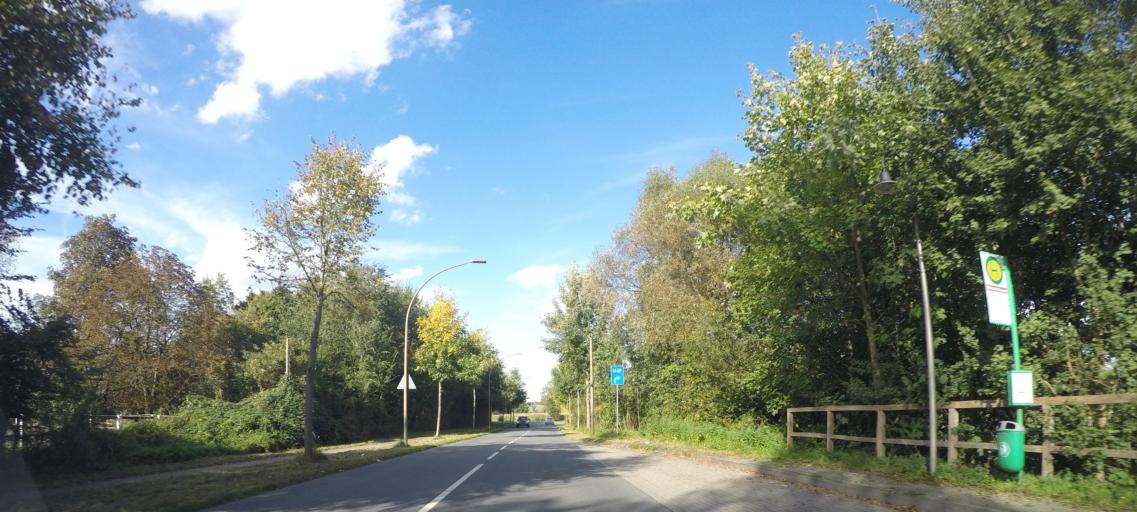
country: DE
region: North Rhine-Westphalia
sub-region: Regierungsbezirk Arnsberg
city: Hamm
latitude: 51.6964
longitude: 7.8828
